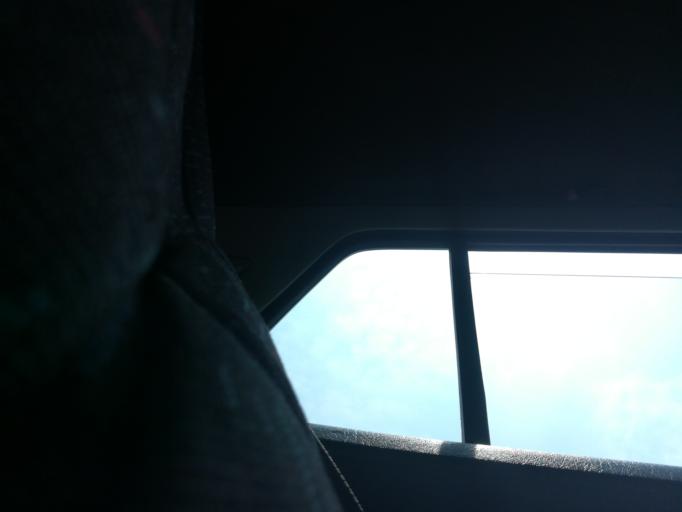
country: NG
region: Lagos
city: Lagos
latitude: 6.4557
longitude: 3.4022
